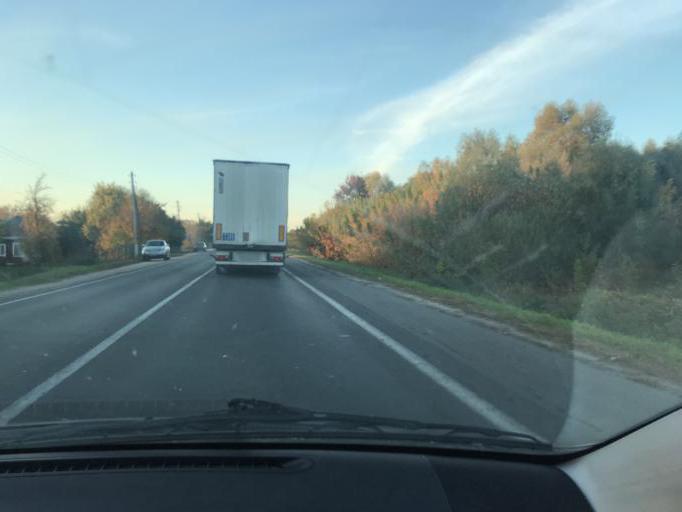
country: BY
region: Brest
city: Pinsk
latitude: 52.1053
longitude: 26.1103
